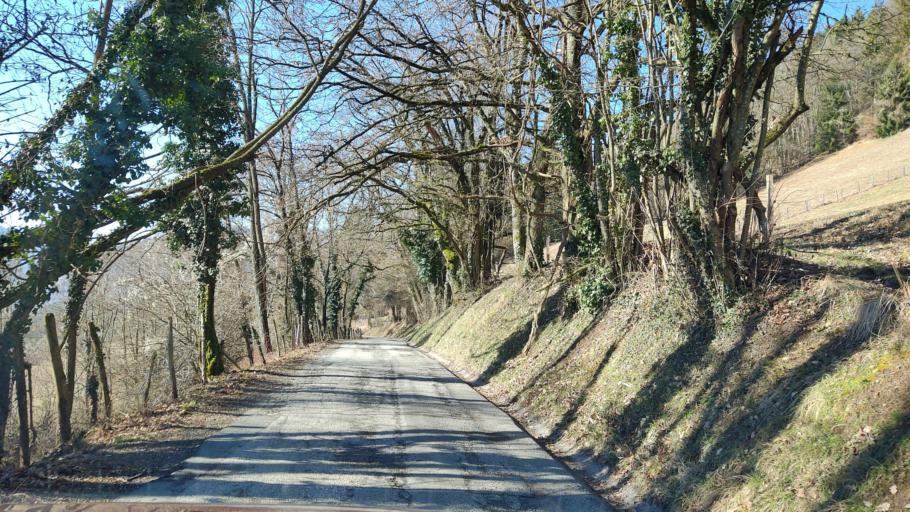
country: FR
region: Rhone-Alpes
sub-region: Departement de la Savoie
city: La Rochette
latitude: 45.4629
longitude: 6.1011
